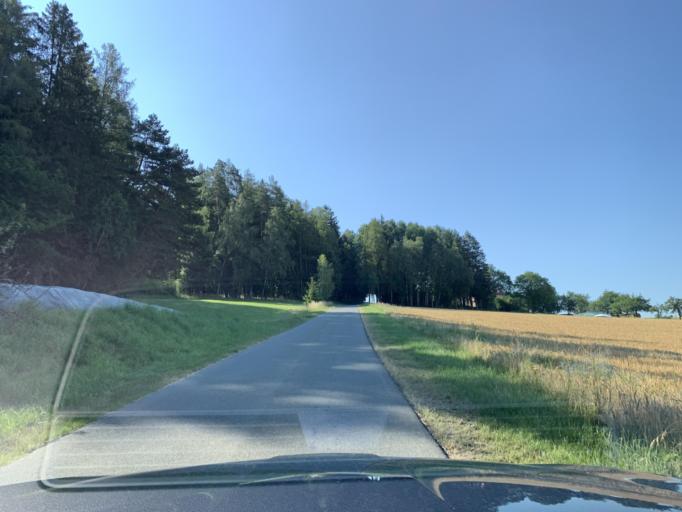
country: DE
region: Bavaria
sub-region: Upper Palatinate
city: Dieterskirchen
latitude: 49.4117
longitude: 12.4336
